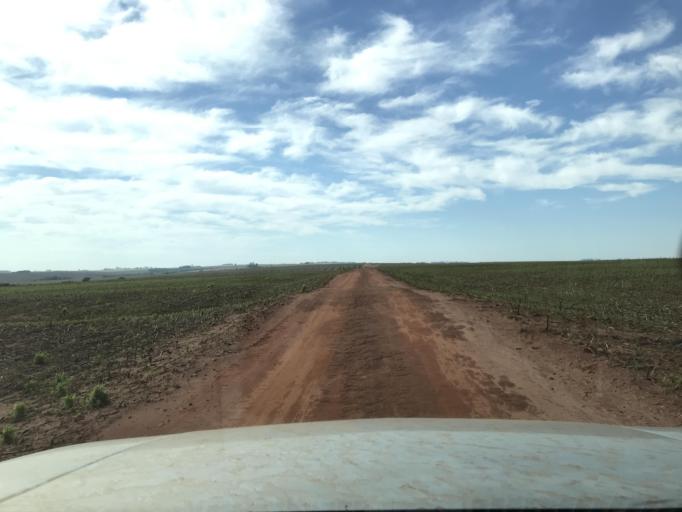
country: BR
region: Parana
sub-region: Palotina
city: Palotina
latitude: -24.1911
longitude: -53.8305
